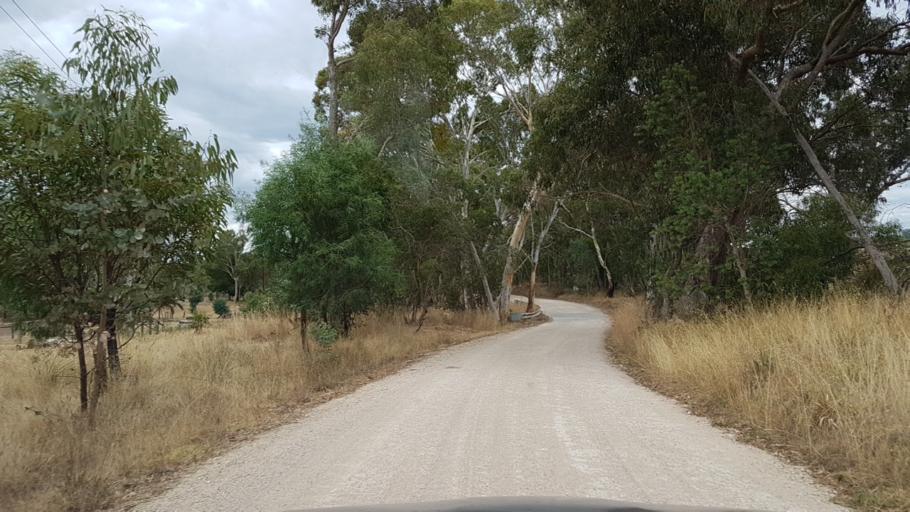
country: AU
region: South Australia
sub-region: Adelaide Hills
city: Gumeracha
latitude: -34.7776
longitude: 138.8639
